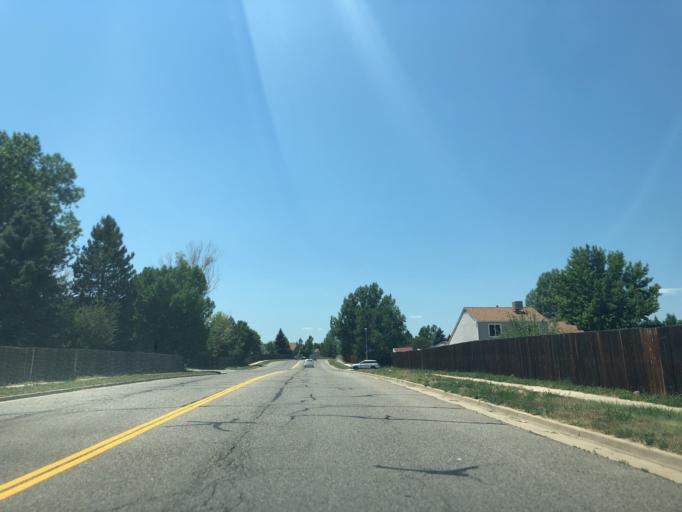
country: US
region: Colorado
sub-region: Arapahoe County
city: Dove Valley
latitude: 39.6265
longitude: -104.7563
